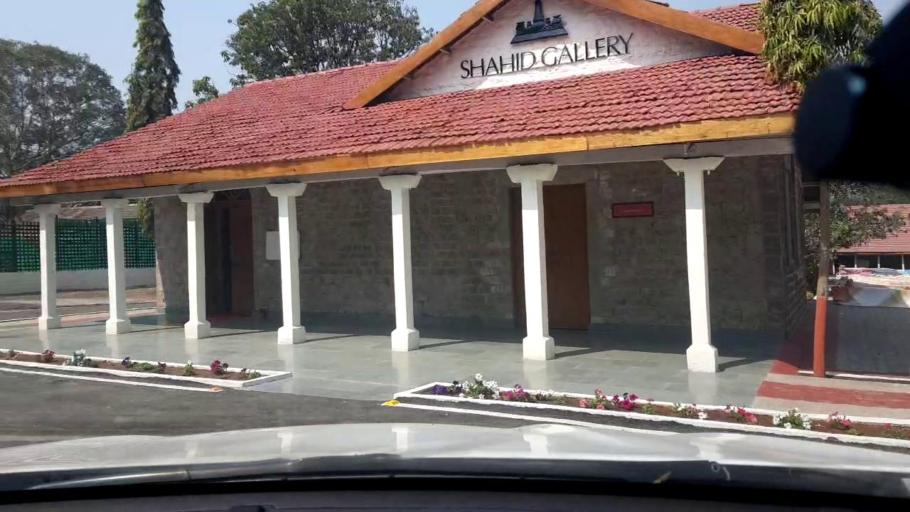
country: IN
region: Maharashtra
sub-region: Pune Division
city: Khadki
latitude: 18.5522
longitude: 73.8630
